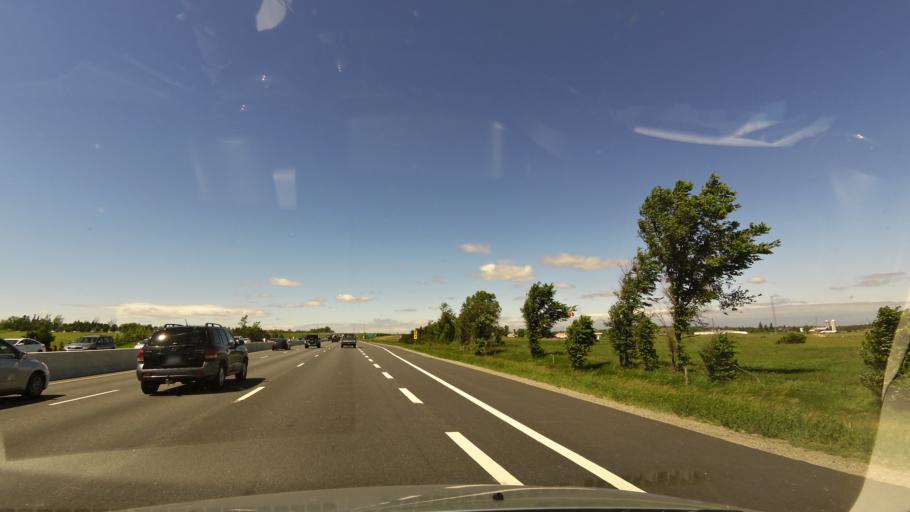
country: CA
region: Ontario
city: Bradford West Gwillimbury
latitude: 44.0937
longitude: -79.6293
